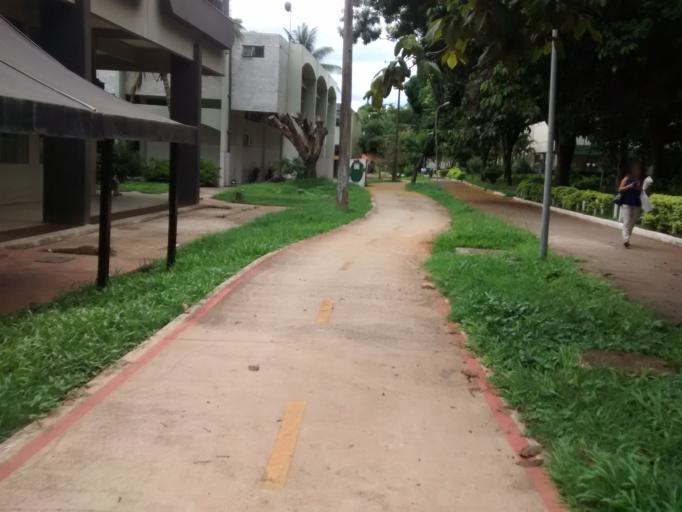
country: BR
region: Federal District
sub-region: Brasilia
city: Brasilia
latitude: -15.7581
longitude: -47.8836
